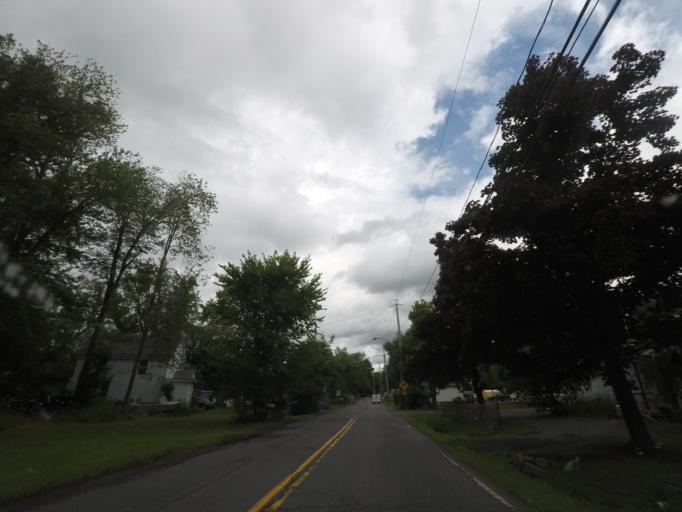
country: US
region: New York
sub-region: Rensselaer County
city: West Sand Lake
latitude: 42.6652
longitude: -73.6274
